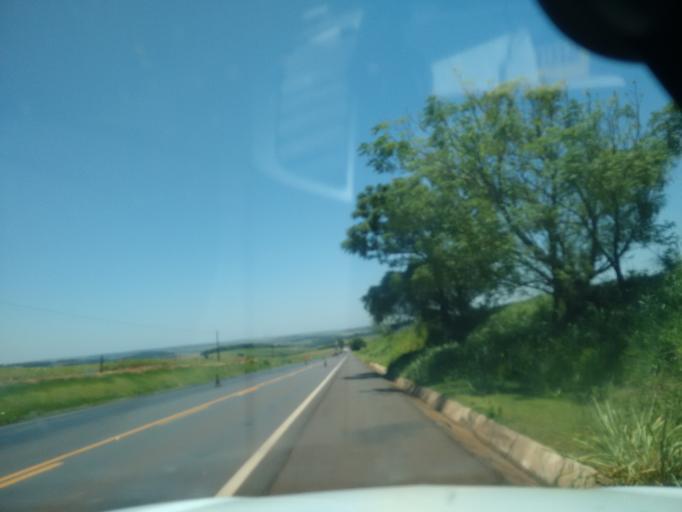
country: BR
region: Parana
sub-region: Marechal Candido Rondon
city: Marechal Candido Rondon
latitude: -24.4444
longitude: -54.1629
